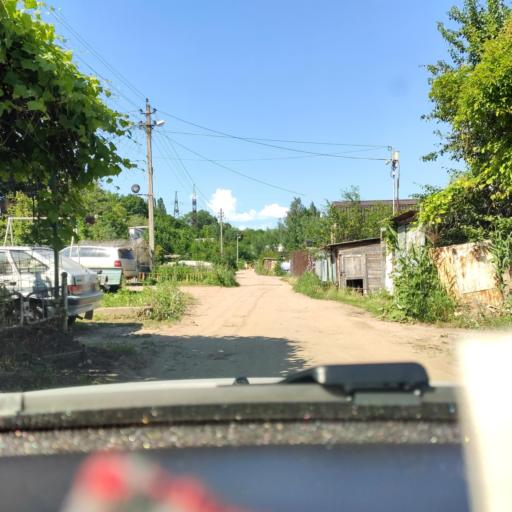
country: RU
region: Voronezj
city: Voronezh
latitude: 51.6206
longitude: 39.1925
